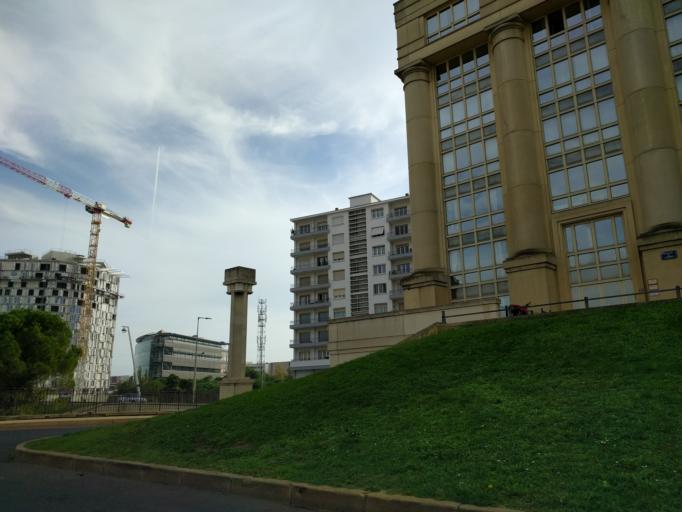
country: FR
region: Languedoc-Roussillon
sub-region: Departement de l'Herault
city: Montpellier
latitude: 43.6068
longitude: 3.8958
